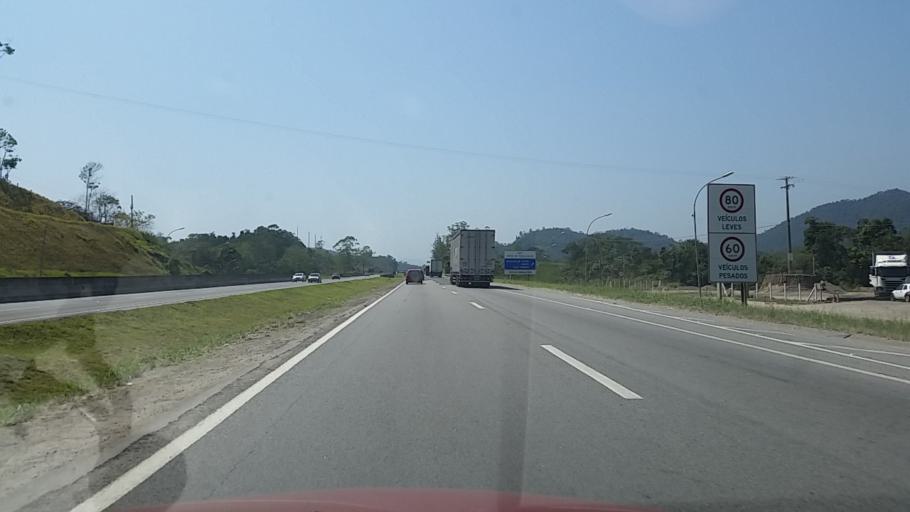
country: BR
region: Sao Paulo
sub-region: Miracatu
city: Miracatu
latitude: -24.2720
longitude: -47.4043
